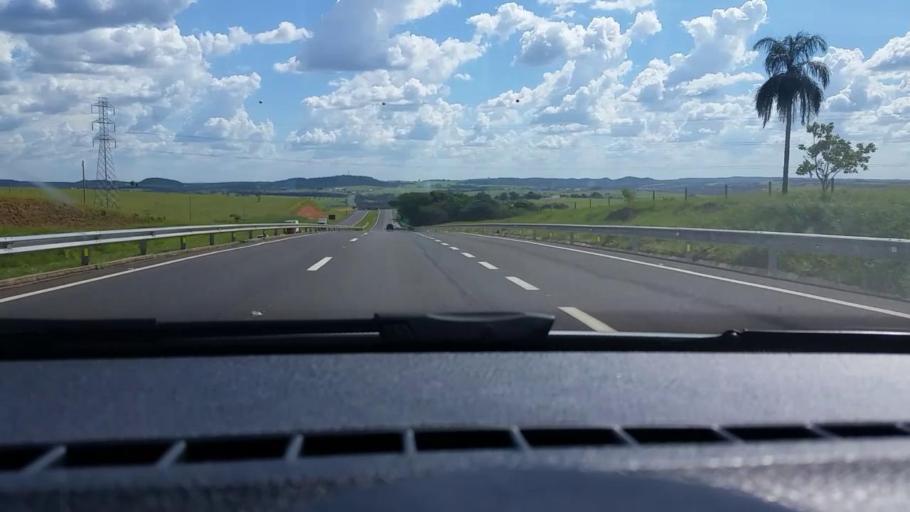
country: BR
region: Sao Paulo
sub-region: Bauru
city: Bauru
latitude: -22.3918
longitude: -49.0795
